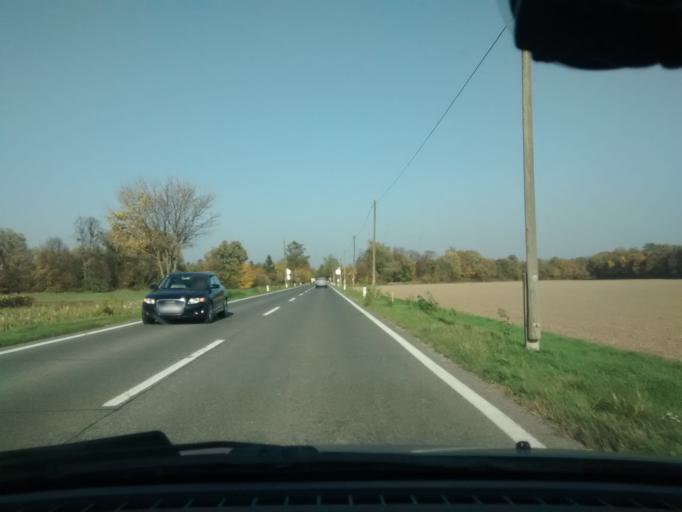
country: AT
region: Lower Austria
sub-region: Politischer Bezirk Modling
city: Achau
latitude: 48.0769
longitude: 16.3884
